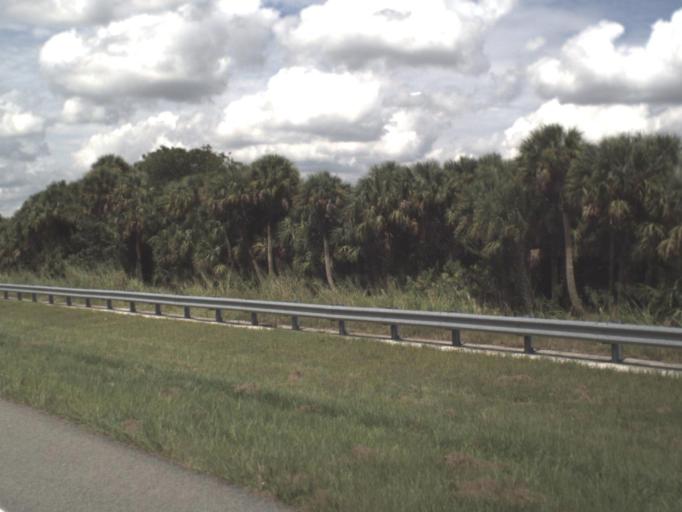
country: US
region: Florida
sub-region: Collier County
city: Immokalee
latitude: 26.3837
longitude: -81.3699
